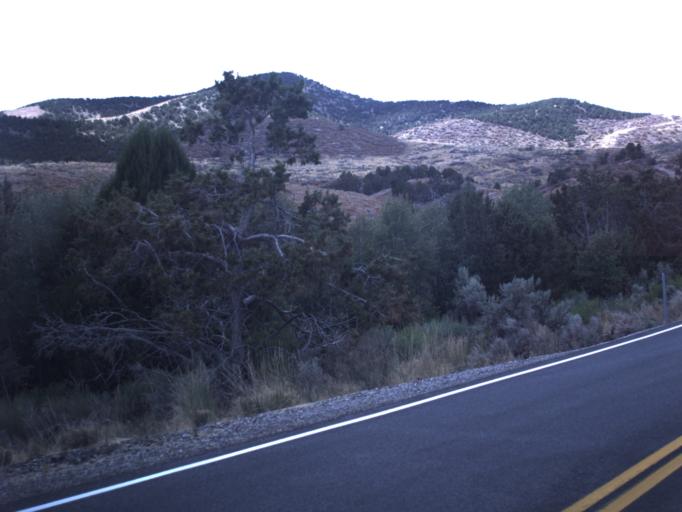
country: US
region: Utah
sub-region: Tooele County
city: Grantsville
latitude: 40.3376
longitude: -112.5330
